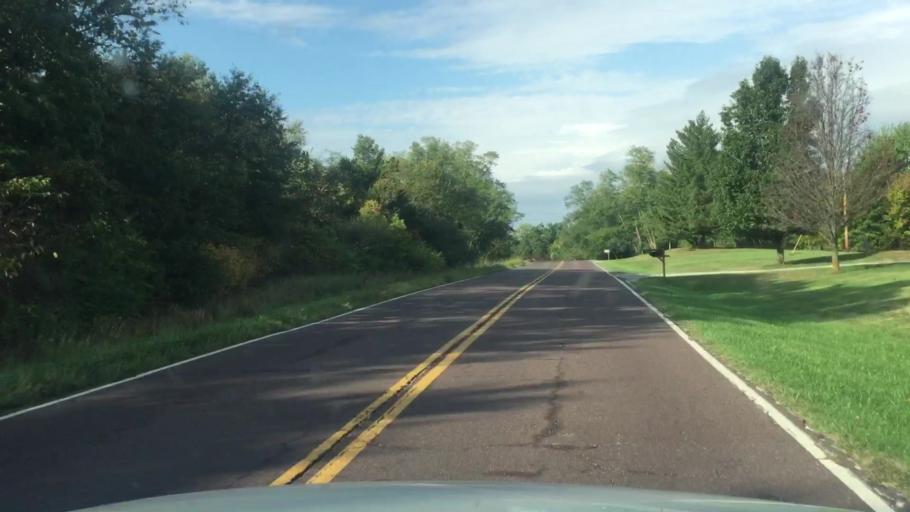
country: US
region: Missouri
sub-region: Boone County
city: Columbia
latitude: 38.8647
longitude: -92.3082
